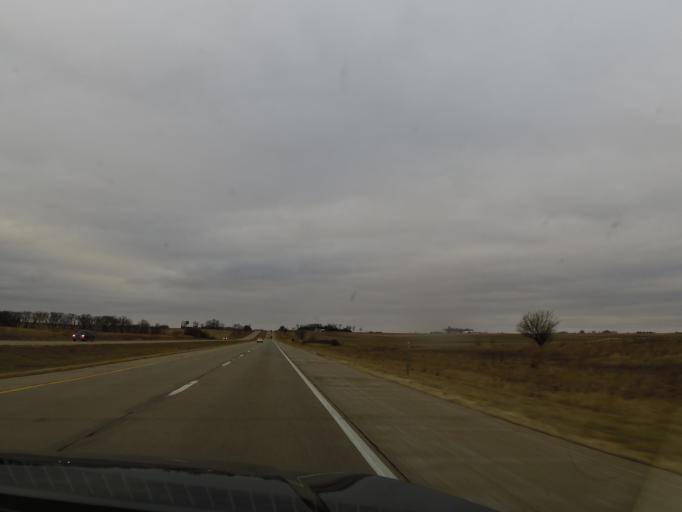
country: US
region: Iowa
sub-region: Buchanan County
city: Jesup
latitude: 42.3352
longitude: -92.0144
